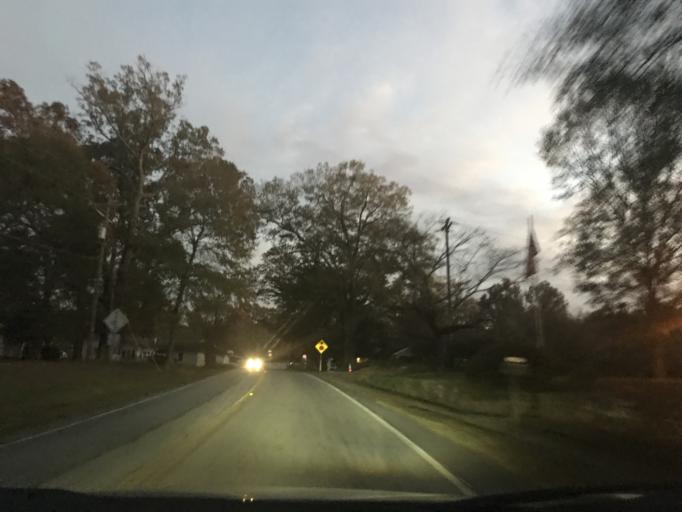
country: US
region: South Carolina
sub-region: Spartanburg County
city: Mayo
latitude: 35.0478
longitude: -81.8910
